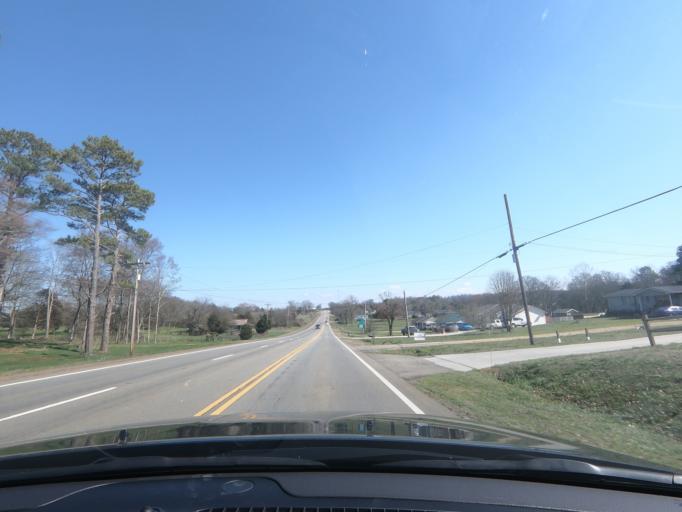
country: US
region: Georgia
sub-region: Bartow County
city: Adairsville
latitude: 34.4484
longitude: -84.8391
